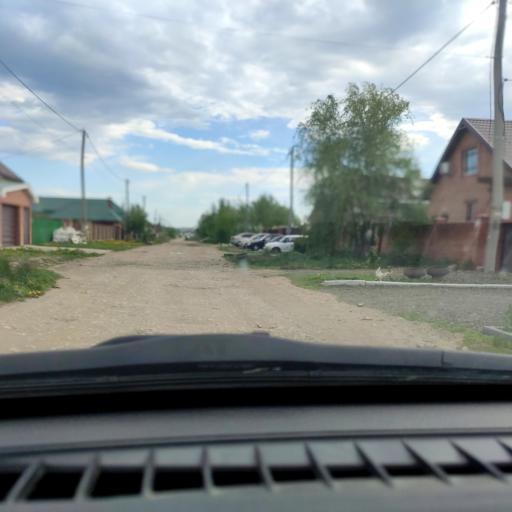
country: RU
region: Samara
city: Tol'yatti
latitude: 53.5734
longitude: 49.4116
